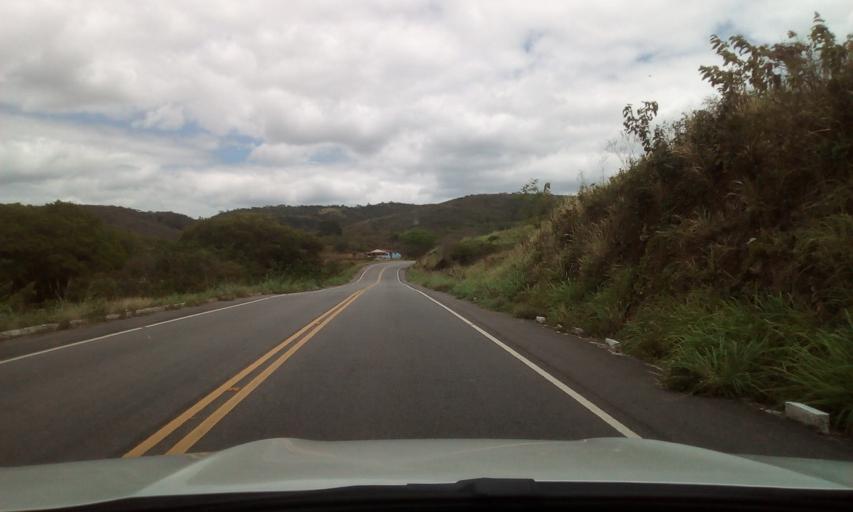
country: BR
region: Paraiba
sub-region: Serra Redonda
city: Alagoa Grande
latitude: -7.1539
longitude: -35.6092
